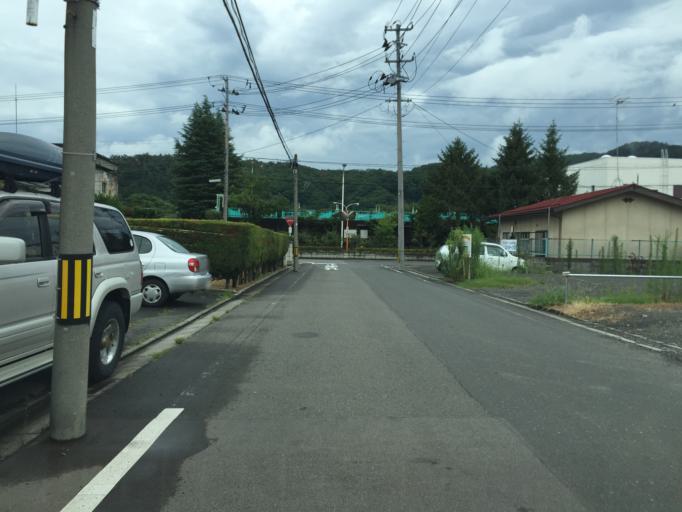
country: JP
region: Fukushima
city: Fukushima-shi
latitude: 37.7667
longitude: 140.4876
